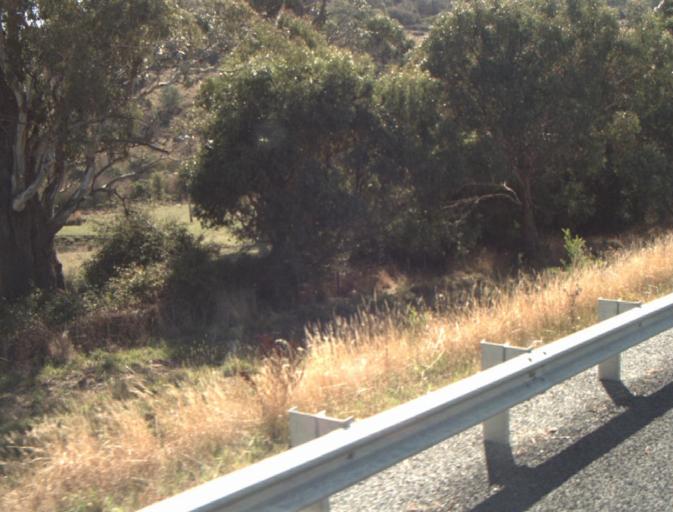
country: AU
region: Tasmania
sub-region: Launceston
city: Mayfield
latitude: -41.3648
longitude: 147.1080
